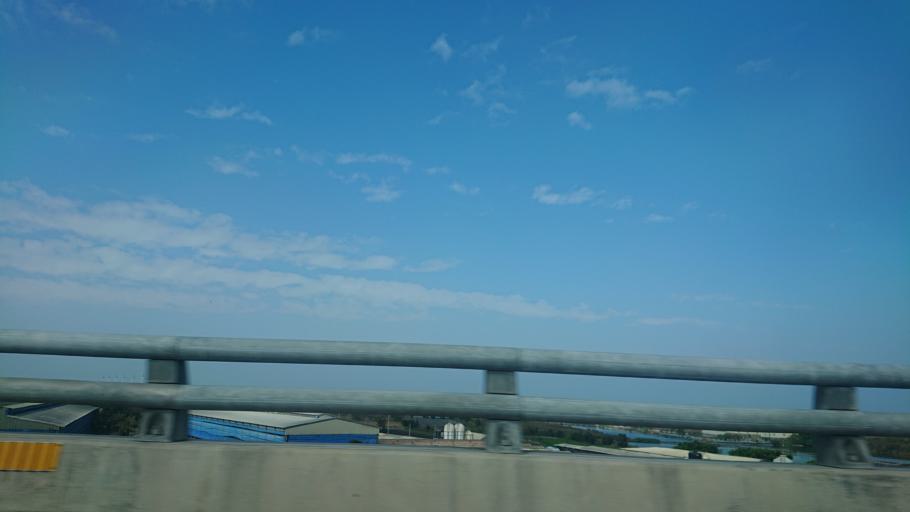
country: TW
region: Taiwan
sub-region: Changhua
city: Chang-hua
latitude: 23.9860
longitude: 120.3680
